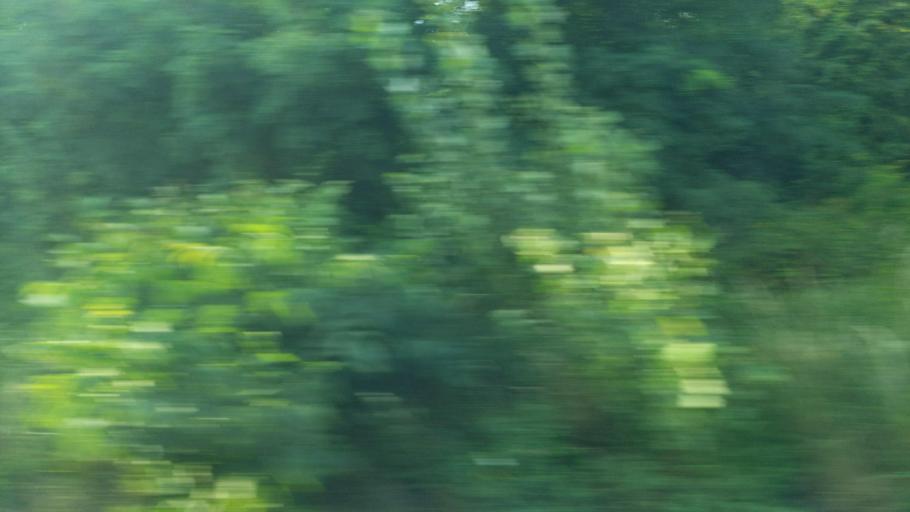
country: CZ
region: Praha
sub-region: Praha 14
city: Dolni Pocernice
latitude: 50.0824
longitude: 14.5965
